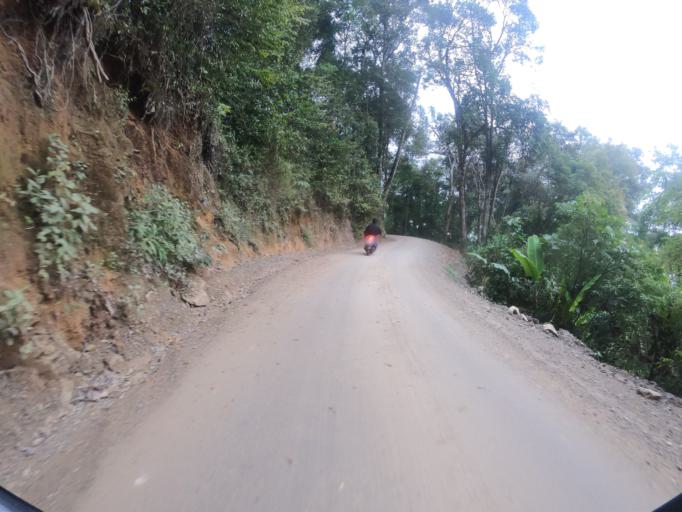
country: TH
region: Chiang Mai
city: Chiang Mai
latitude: 18.8165
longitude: 98.8944
